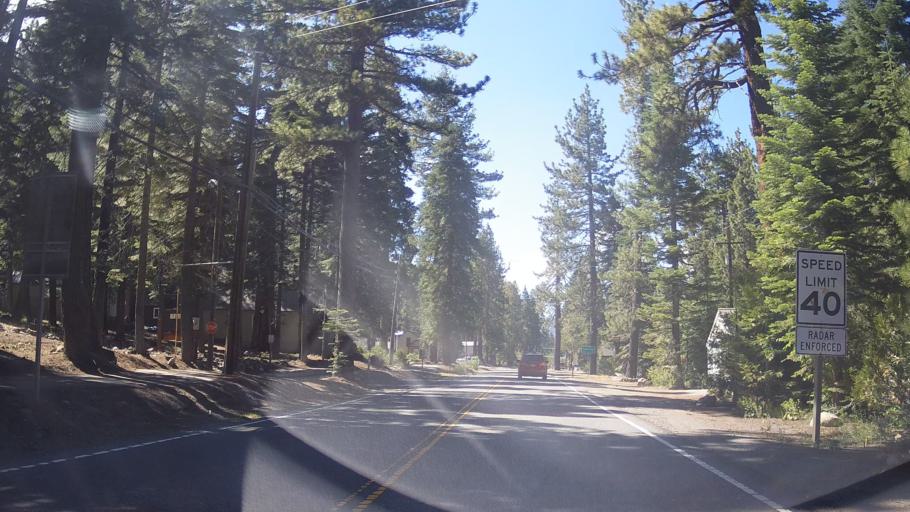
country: US
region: California
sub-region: Placer County
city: Tahoma
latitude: 39.0643
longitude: -120.1249
